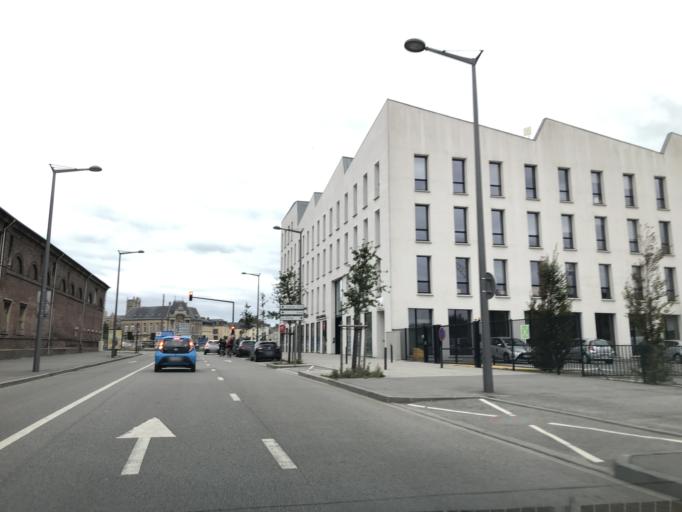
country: FR
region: Haute-Normandie
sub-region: Departement de la Seine-Maritime
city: Dieppe
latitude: 49.9219
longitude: 1.0837
